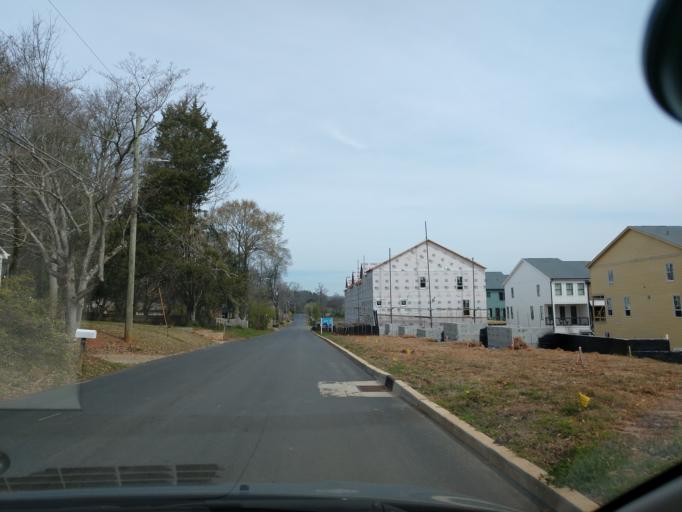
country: US
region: Georgia
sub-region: Fulton County
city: Atlanta
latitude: 33.7233
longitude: -84.3633
